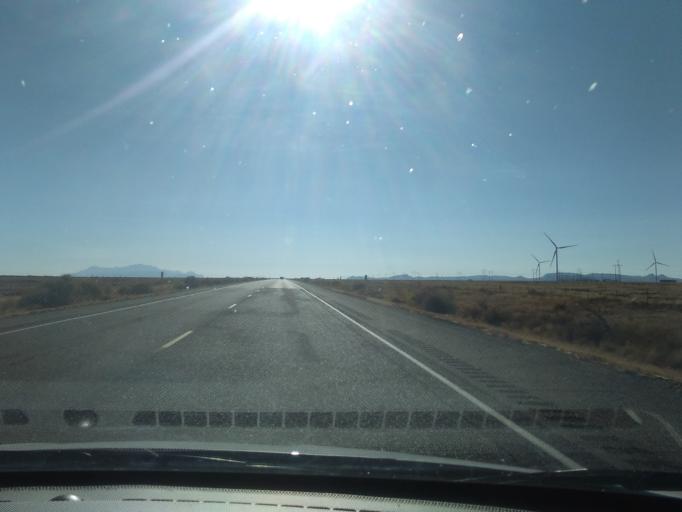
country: US
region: New Mexico
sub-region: Dona Ana County
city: Hatch
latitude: 32.5458
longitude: -107.4800
